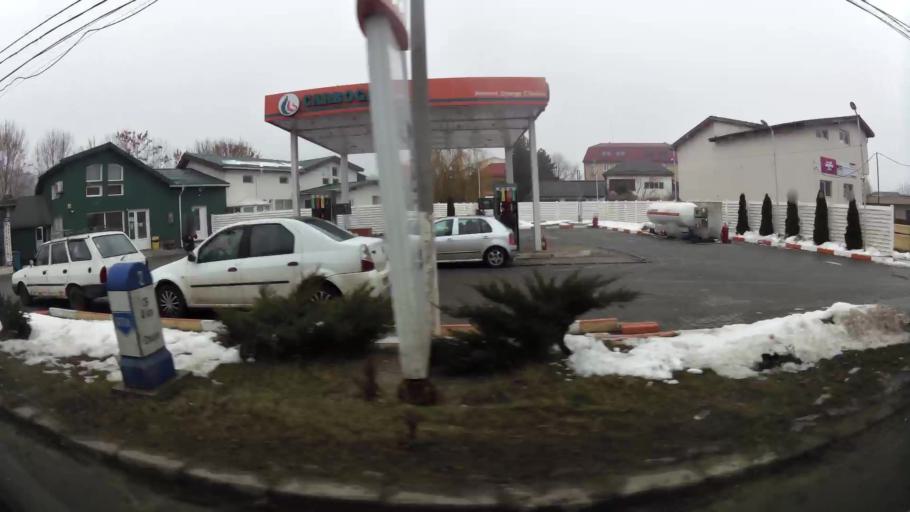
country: RO
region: Ilfov
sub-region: Comuna Chiajna
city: Rosu
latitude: 44.4517
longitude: 26.0013
